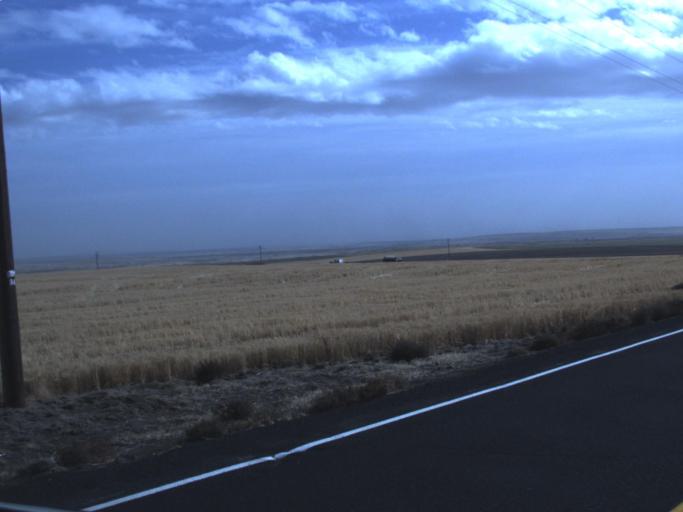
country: US
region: Washington
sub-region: Okanogan County
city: Coulee Dam
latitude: 47.5988
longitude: -118.7862
